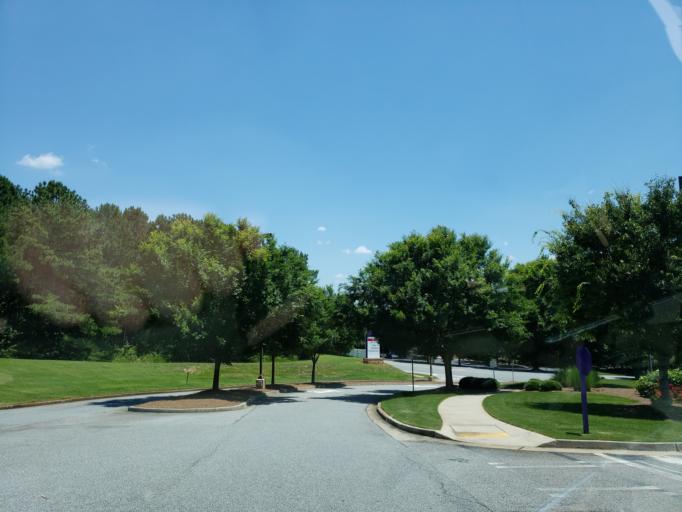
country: US
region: Georgia
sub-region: Fulton County
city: Alpharetta
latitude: 34.0617
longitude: -84.3197
